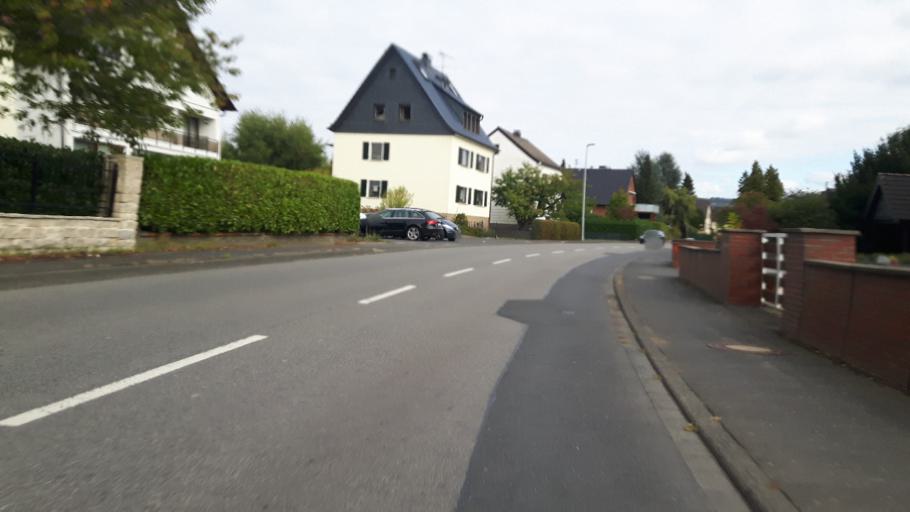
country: DE
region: North Rhine-Westphalia
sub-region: Regierungsbezirk Koln
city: Eitorf
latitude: 50.7778
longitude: 7.4633
